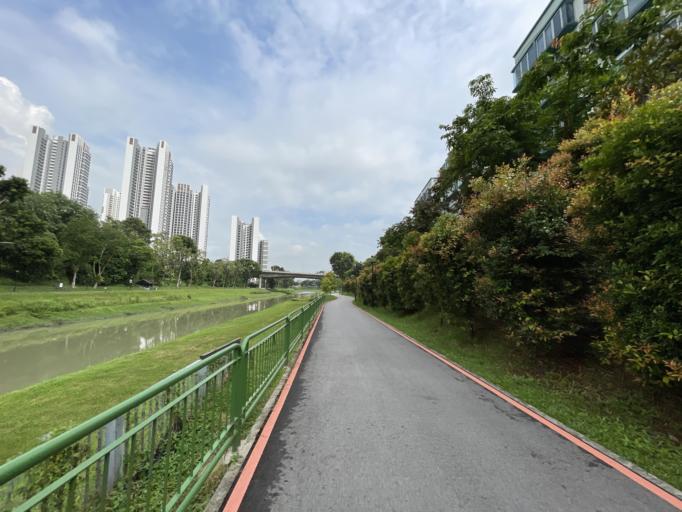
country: SG
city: Singapore
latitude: 1.3234
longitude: 103.7664
